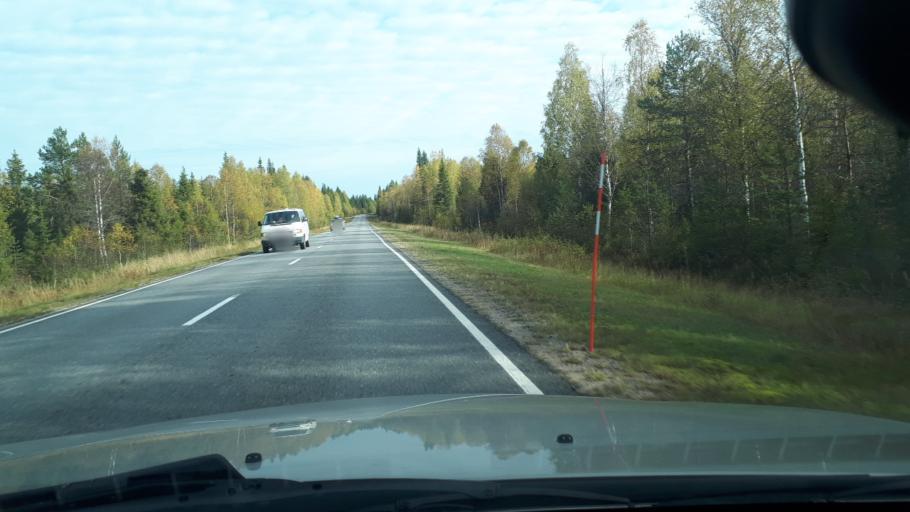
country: FI
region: Northern Ostrobothnia
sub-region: Oulu
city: Yli-Ii
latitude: 65.9469
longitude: 25.9021
